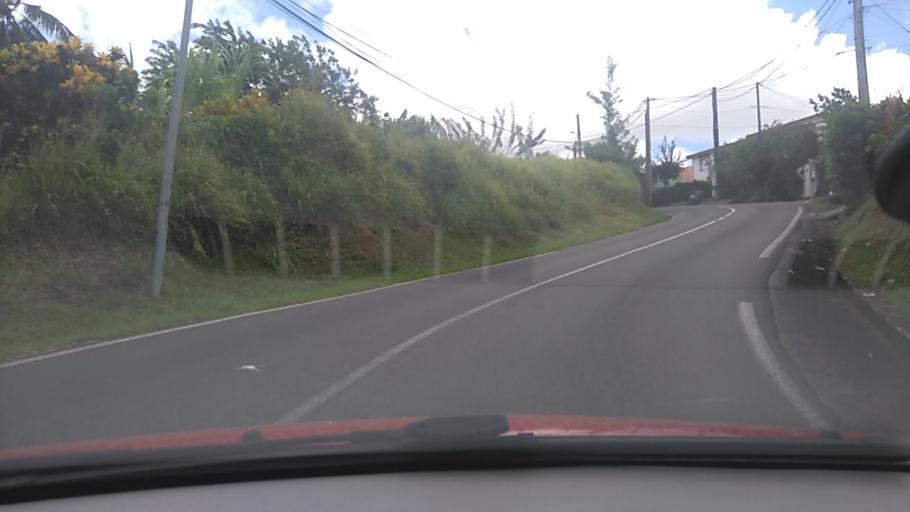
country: MQ
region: Martinique
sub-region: Martinique
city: Saint-Esprit
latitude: 14.5661
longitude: -60.9433
